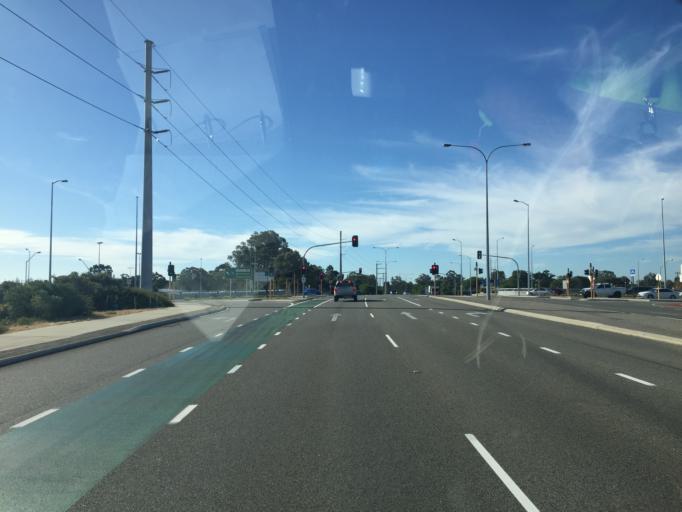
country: AU
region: Western Australia
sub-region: Belmont
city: Kewdale
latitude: -31.9744
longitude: 115.9501
